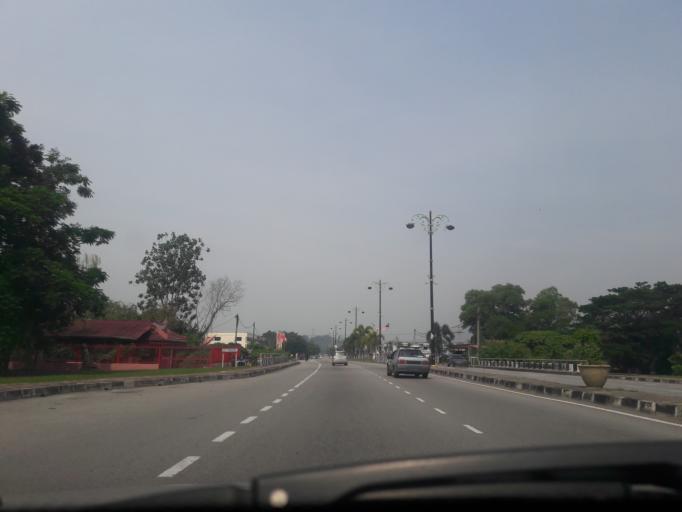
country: MY
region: Kedah
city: Kulim
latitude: 5.3874
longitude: 100.5607
